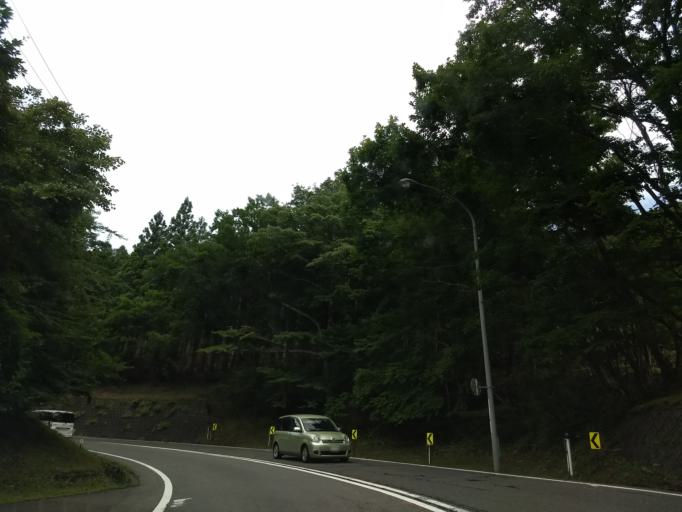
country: JP
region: Shizuoka
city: Gotemba
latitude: 35.3819
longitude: 138.8587
